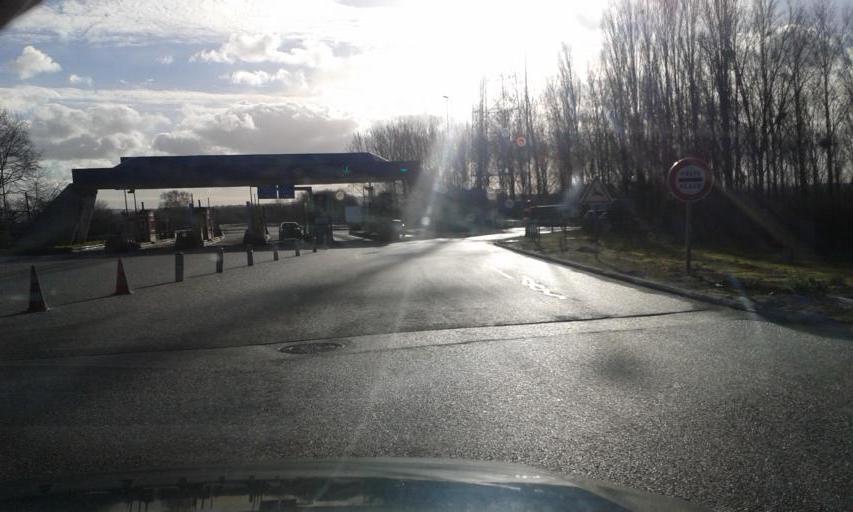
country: FR
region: Picardie
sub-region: Departement de l'Oise
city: Remy
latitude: 49.3997
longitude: 2.6992
